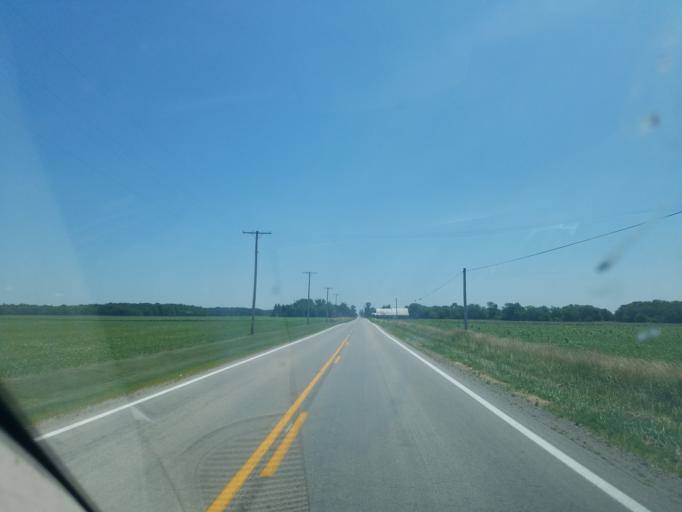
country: US
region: Ohio
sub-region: Mercer County
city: Rockford
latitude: 40.7425
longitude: -84.7343
